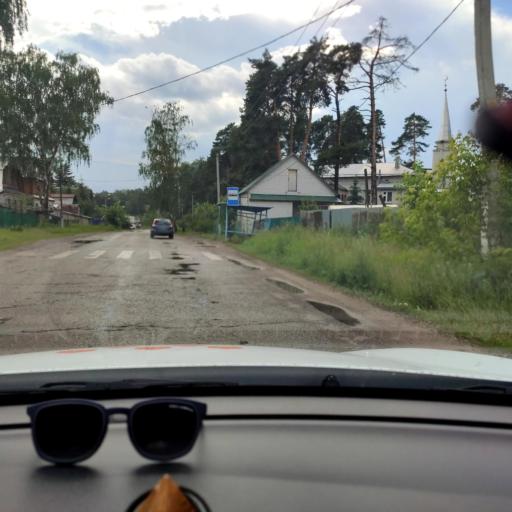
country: RU
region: Tatarstan
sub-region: Zelenodol'skiy Rayon
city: Vasil'yevo
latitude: 55.8323
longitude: 48.7068
